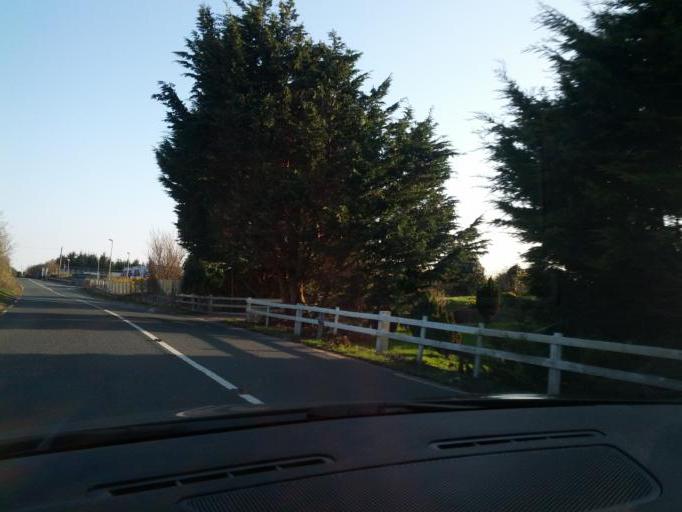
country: IE
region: Connaught
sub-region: County Galway
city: Oughterard
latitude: 53.2939
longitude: -9.5503
